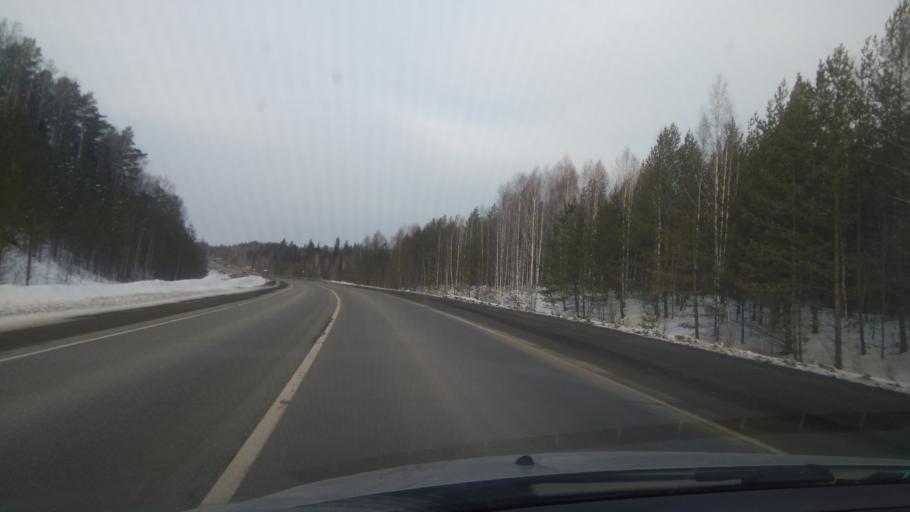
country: RU
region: Sverdlovsk
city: Bisert'
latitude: 56.8377
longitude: 58.8738
